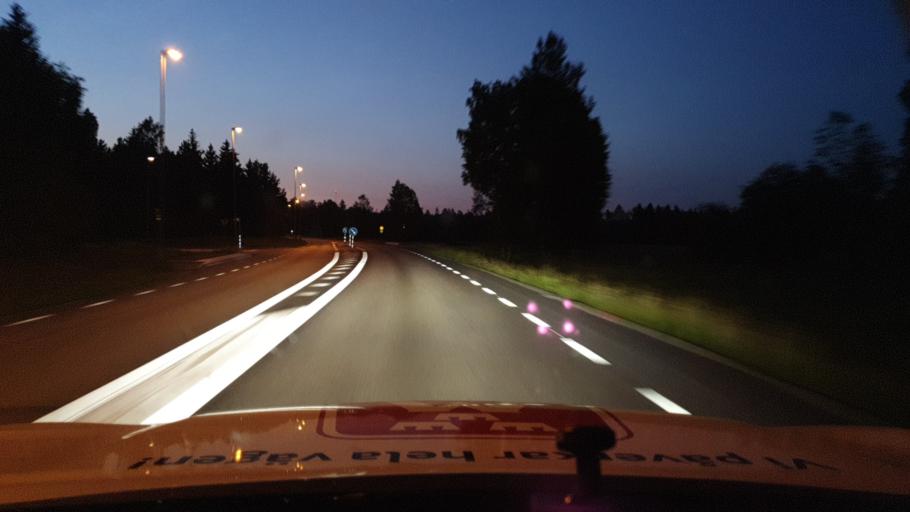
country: SE
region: OErebro
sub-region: Karlskoga Kommun
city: Karlskoga
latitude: 59.3420
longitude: 14.5789
